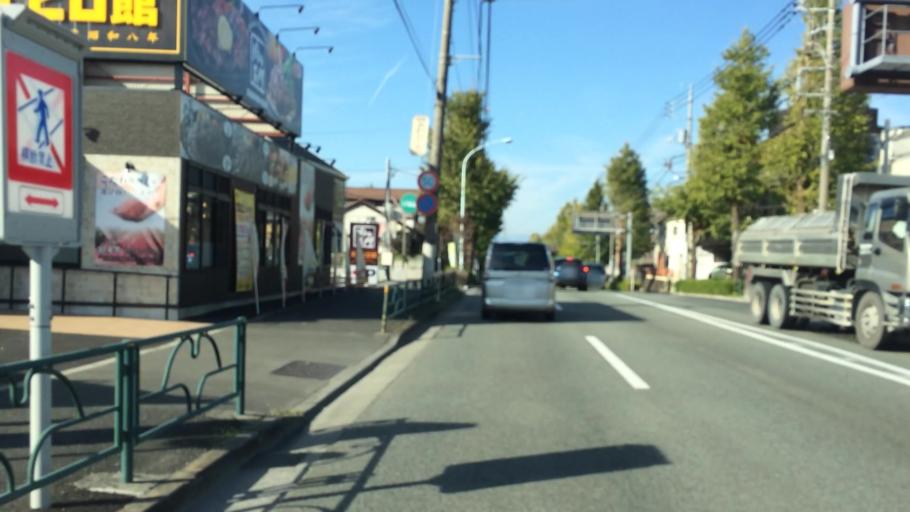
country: JP
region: Tokyo
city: Hino
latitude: 35.6868
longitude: 139.4140
